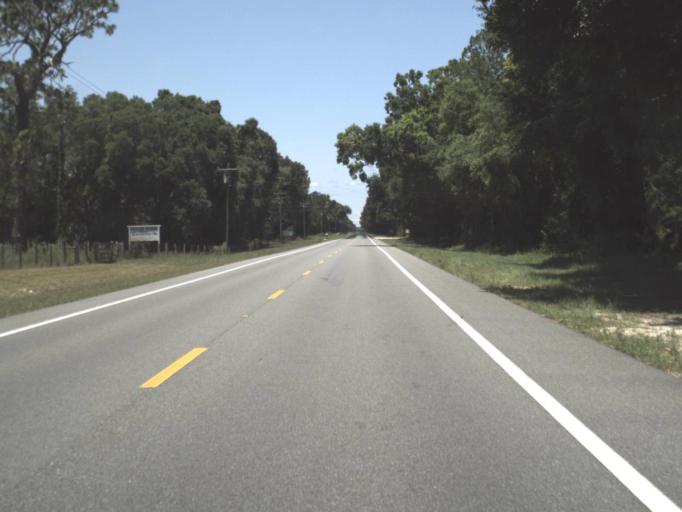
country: US
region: Florida
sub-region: Dixie County
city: Cross City
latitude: 29.7134
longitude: -82.9845
